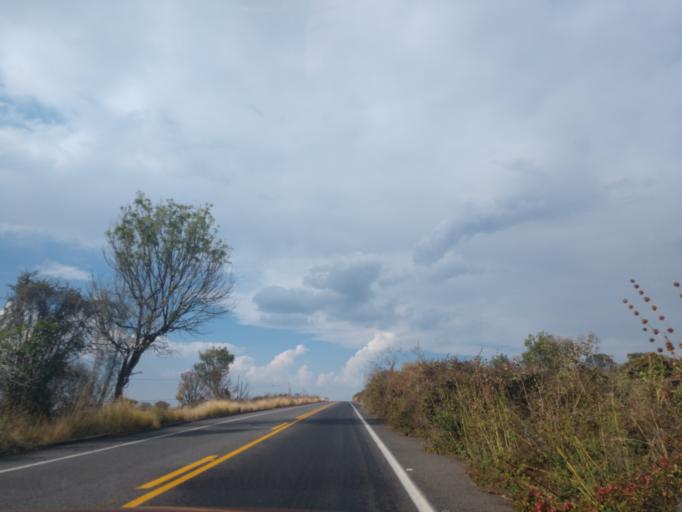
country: MX
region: Jalisco
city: La Manzanilla de la Paz
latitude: 20.0695
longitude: -103.1712
